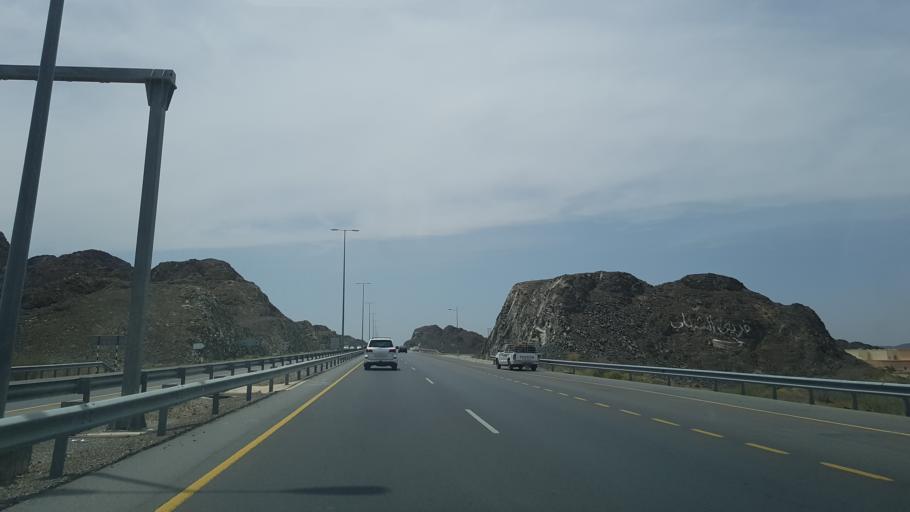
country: OM
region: Muhafazat ad Dakhiliyah
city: Izki
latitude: 22.9247
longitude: 57.7848
